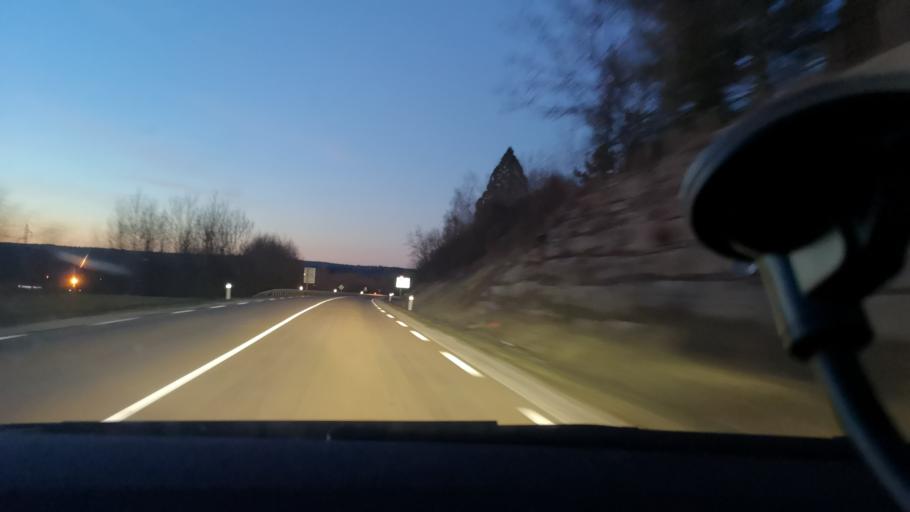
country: FR
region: Franche-Comte
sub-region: Departement du Jura
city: Champagnole
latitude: 46.7549
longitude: 5.9130
